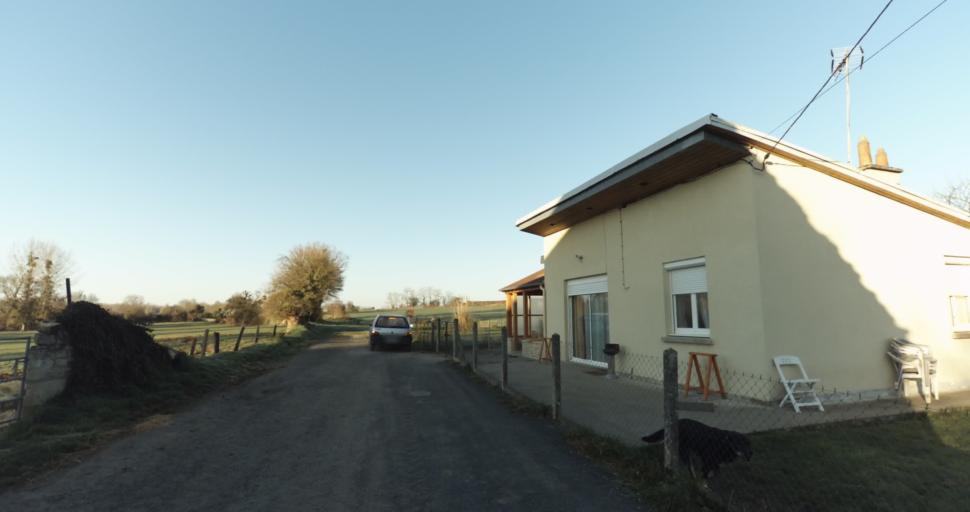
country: FR
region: Lower Normandy
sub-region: Departement du Calvados
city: Saint-Pierre-sur-Dives
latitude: 49.0149
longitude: -0.0488
